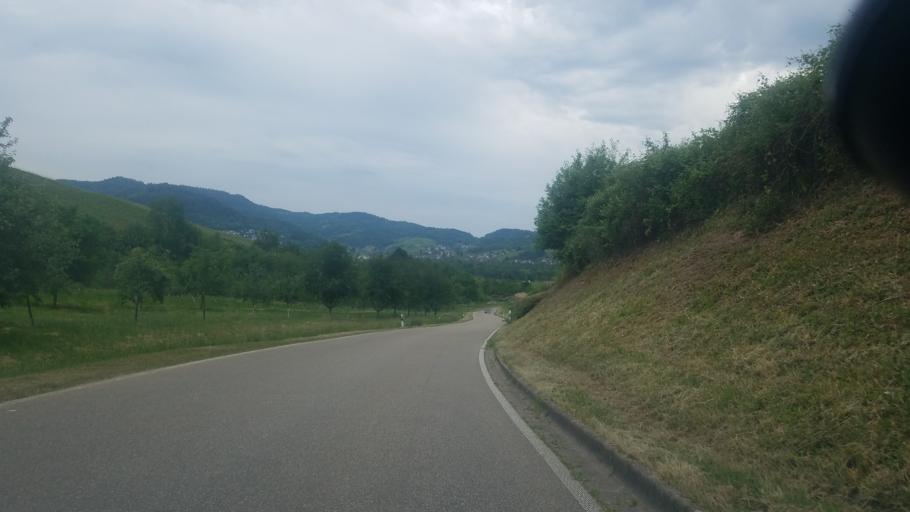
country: DE
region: Baden-Wuerttemberg
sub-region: Freiburg Region
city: Kappelrodeck
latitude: 48.6091
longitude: 8.1106
